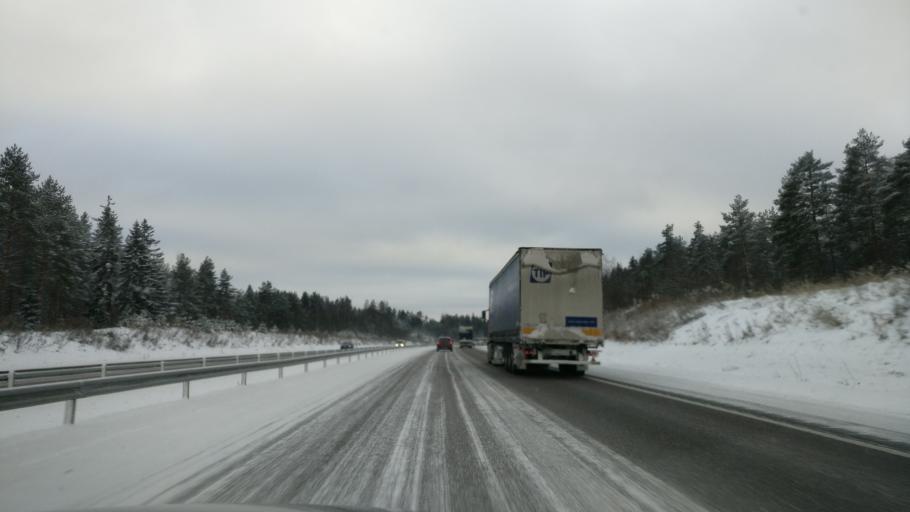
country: FI
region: Paijanne Tavastia
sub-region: Lahti
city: Nastola
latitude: 61.0150
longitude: 25.8244
